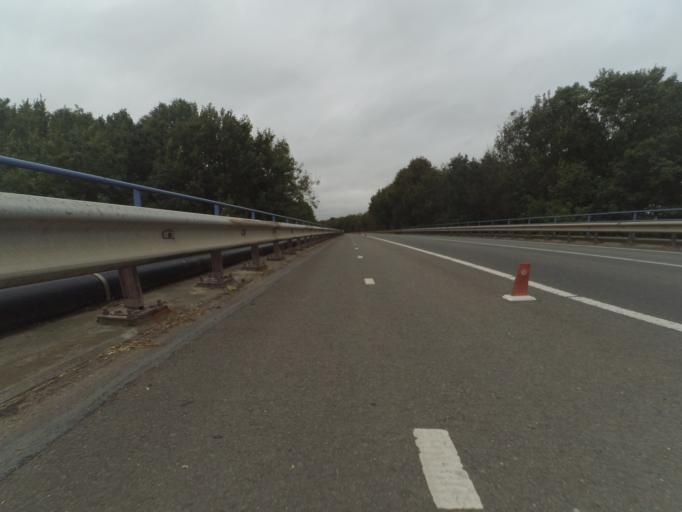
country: NL
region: Gelderland
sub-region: Gemeente Tiel
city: Tiel
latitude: 51.9226
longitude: 5.4252
